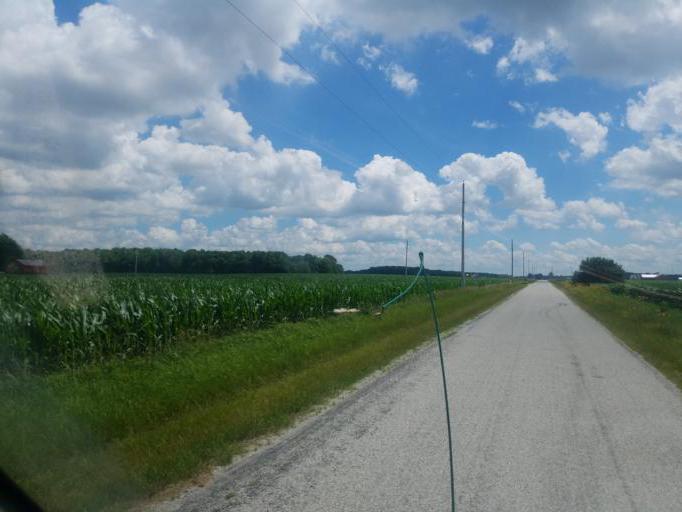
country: US
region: Ohio
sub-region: Huron County
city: Willard
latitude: 40.9859
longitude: -82.8351
